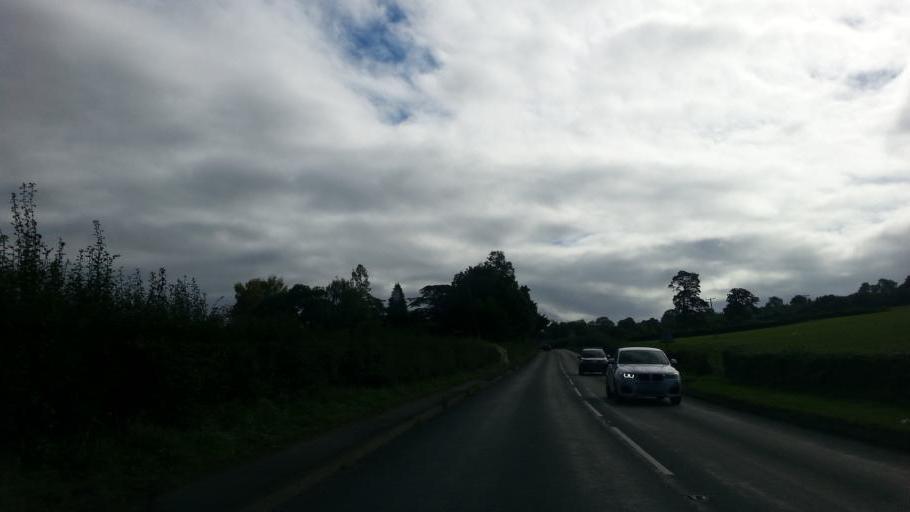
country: GB
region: England
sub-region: Herefordshire
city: Ross on Wye
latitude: 51.9112
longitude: -2.5479
